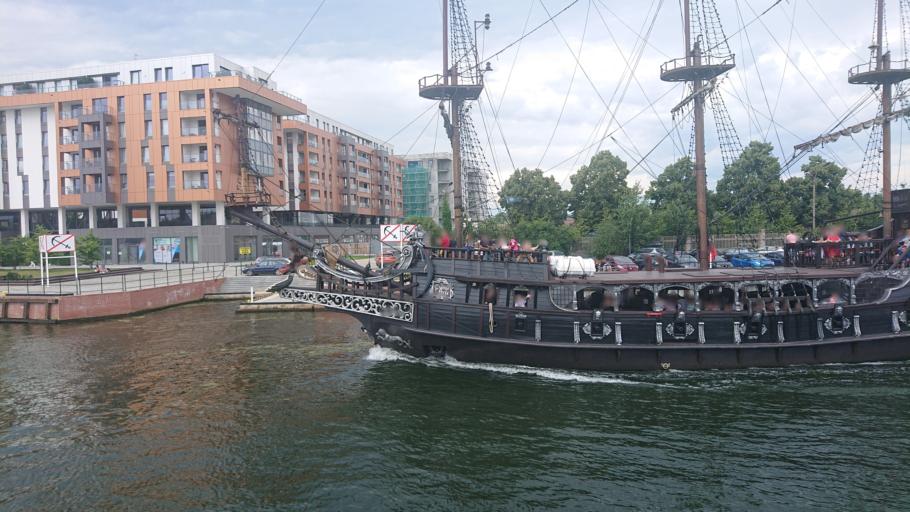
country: PL
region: Pomeranian Voivodeship
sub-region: Gdansk
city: Gdansk
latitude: 54.3550
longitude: 18.6655
